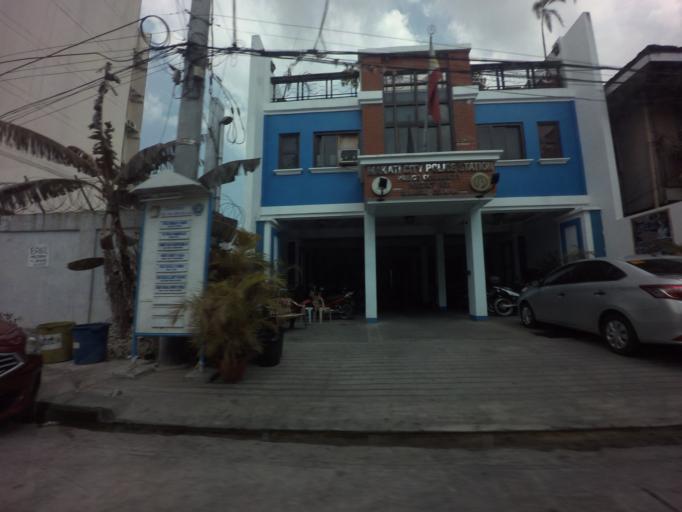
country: PH
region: Metro Manila
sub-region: Mandaluyong
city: Mandaluyong City
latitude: 14.5710
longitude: 121.0213
